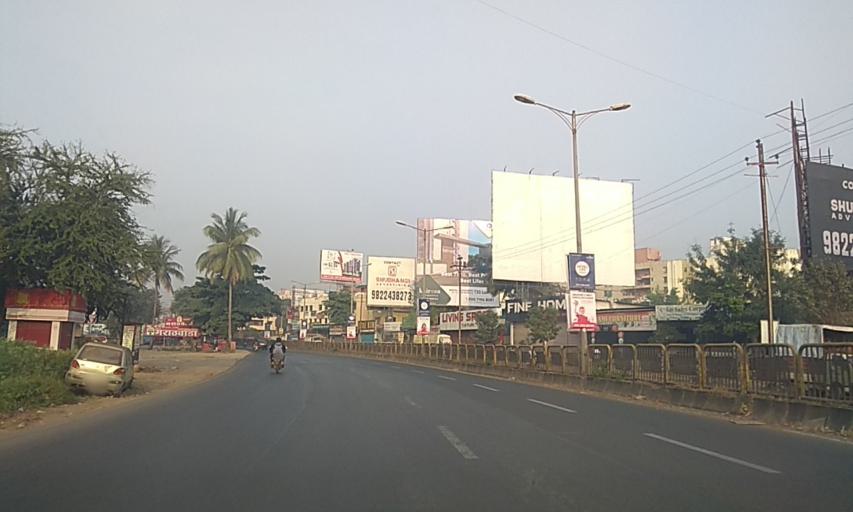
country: IN
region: Maharashtra
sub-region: Pune Division
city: Pimpri
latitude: 18.5918
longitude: 73.7657
